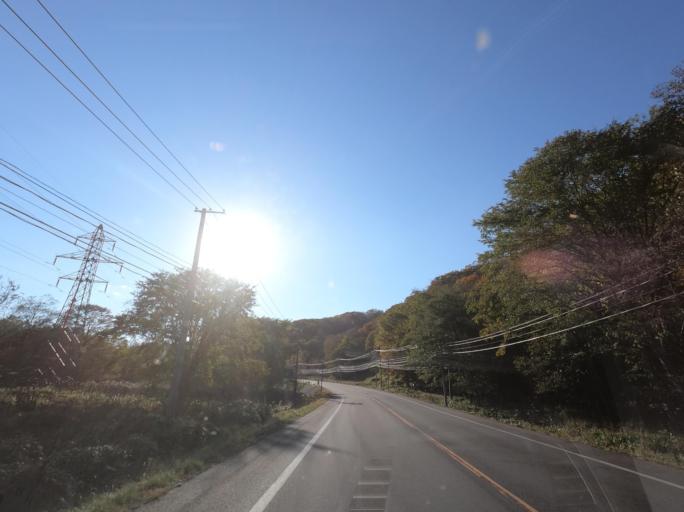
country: JP
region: Hokkaido
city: Kushiro
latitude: 43.3370
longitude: 144.1145
